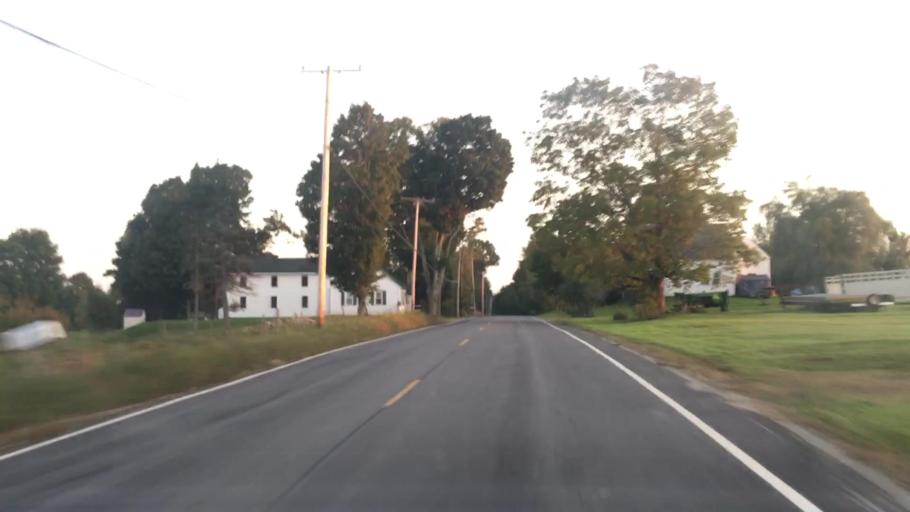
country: US
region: Maine
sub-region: Somerset County
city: Cornville
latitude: 44.8662
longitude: -69.6841
